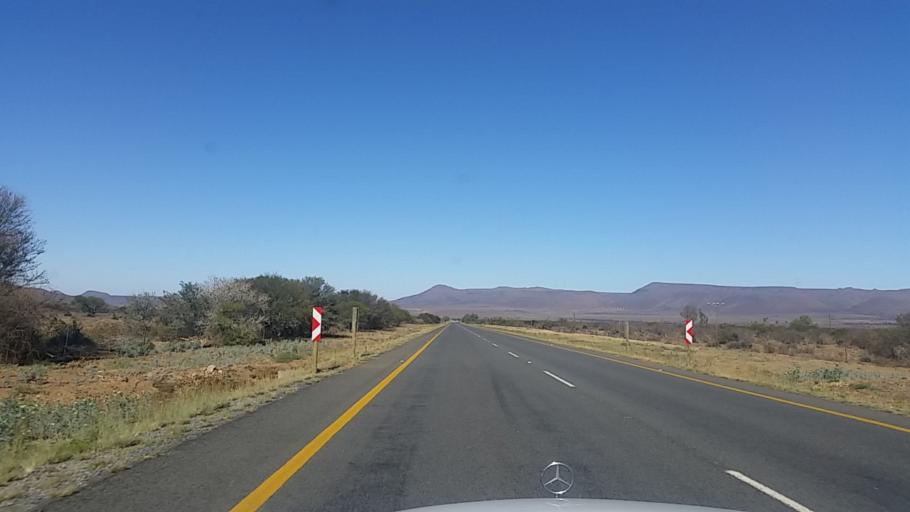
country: ZA
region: Eastern Cape
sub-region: Cacadu District Municipality
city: Graaff-Reinet
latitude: -31.9830
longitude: 24.6965
